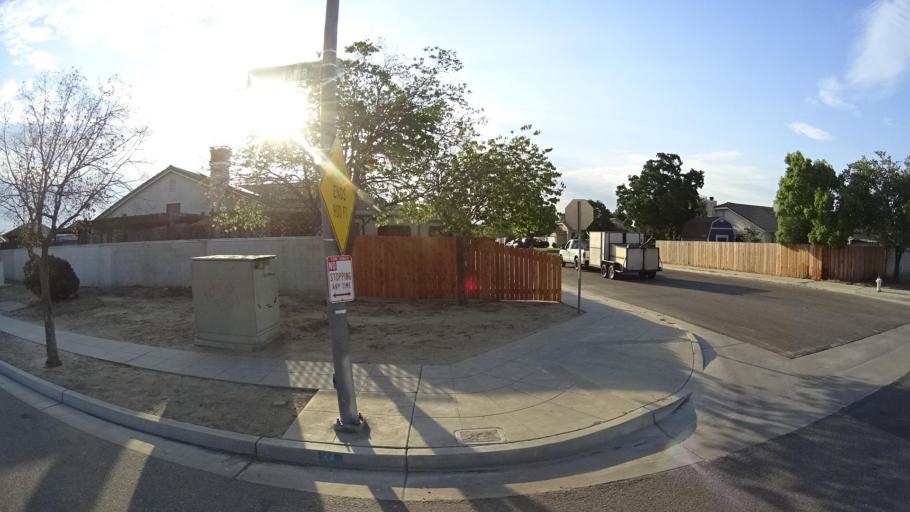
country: US
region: California
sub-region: Fresno County
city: Sunnyside
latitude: 36.7116
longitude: -119.7093
